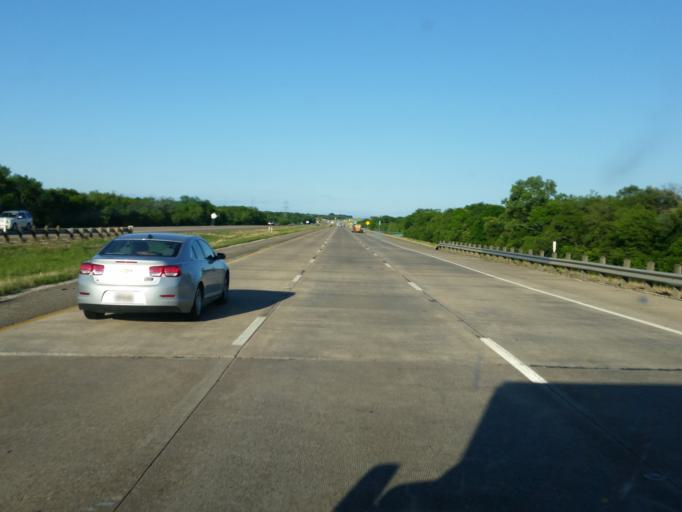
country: US
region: Texas
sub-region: Dallas County
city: Seagoville
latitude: 32.6998
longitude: -96.5303
